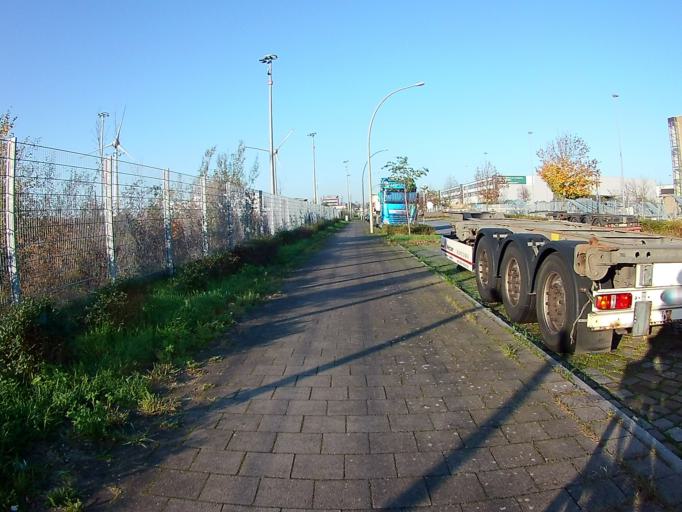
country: DE
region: Hamburg
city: Altona
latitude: 53.5023
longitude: 9.9220
